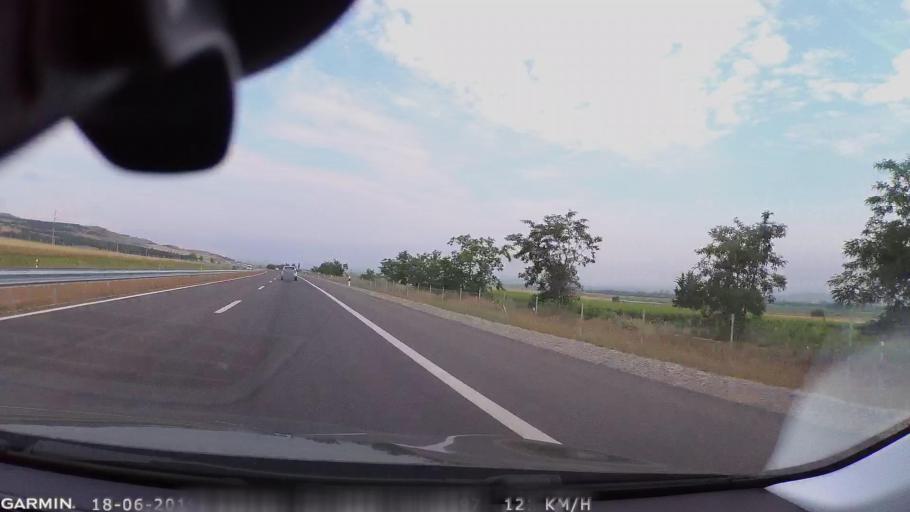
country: MK
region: Stip
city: Shtip
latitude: 41.7948
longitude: 22.0927
